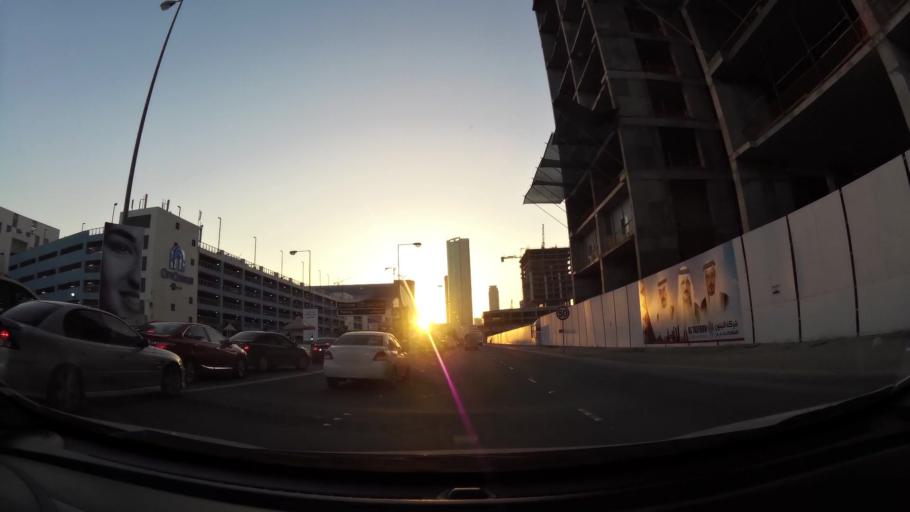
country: BH
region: Manama
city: Jidd Hafs
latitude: 26.2351
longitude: 50.5558
